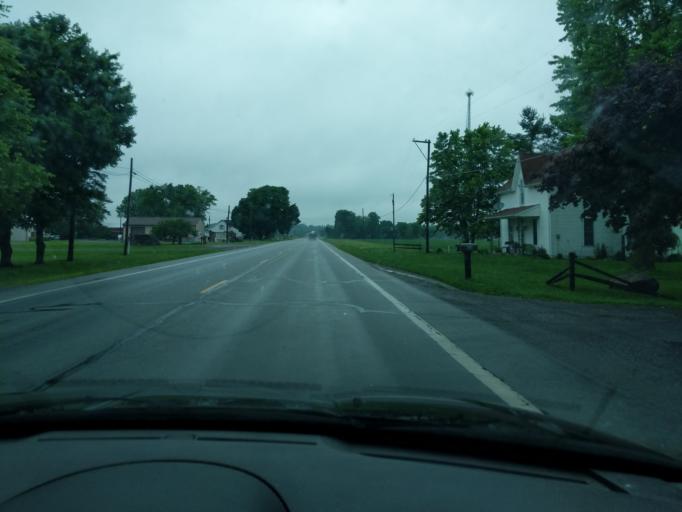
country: US
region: Ohio
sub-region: Logan County
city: West Liberty
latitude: 40.2403
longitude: -83.7526
